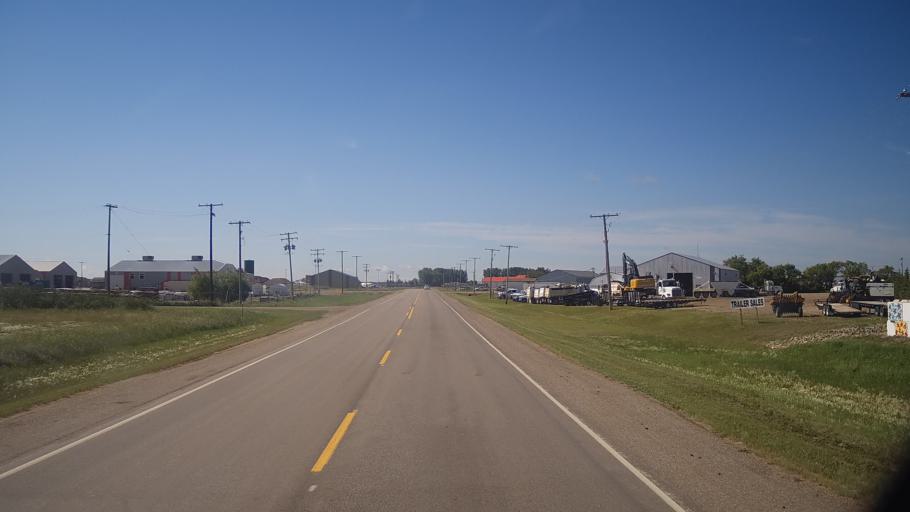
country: CA
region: Saskatchewan
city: Watrous
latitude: 51.6715
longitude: -105.4517
